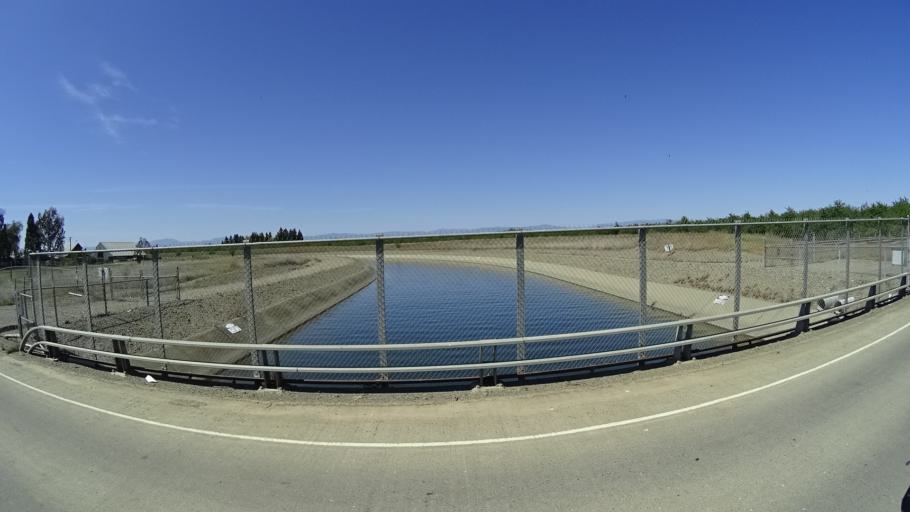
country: US
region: California
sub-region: Glenn County
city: Orland
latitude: 39.7140
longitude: -122.1784
